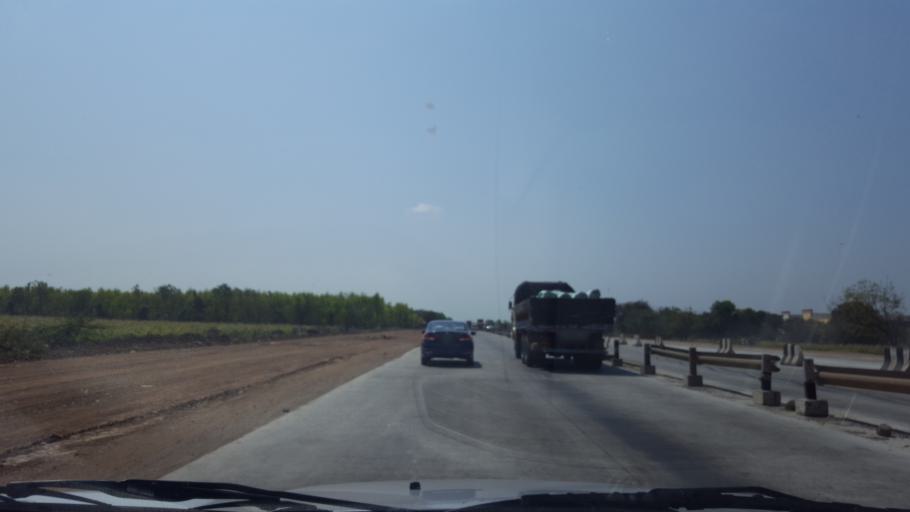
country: IN
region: Andhra Pradesh
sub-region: Prakasam
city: Addanki
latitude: 15.7965
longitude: 80.0392
